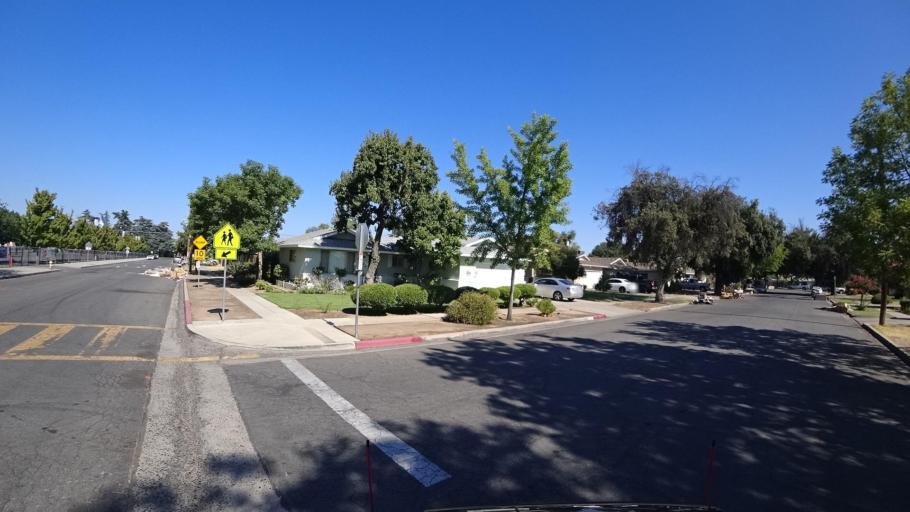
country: US
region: California
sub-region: Fresno County
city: Fresno
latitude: 36.7851
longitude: -119.7520
